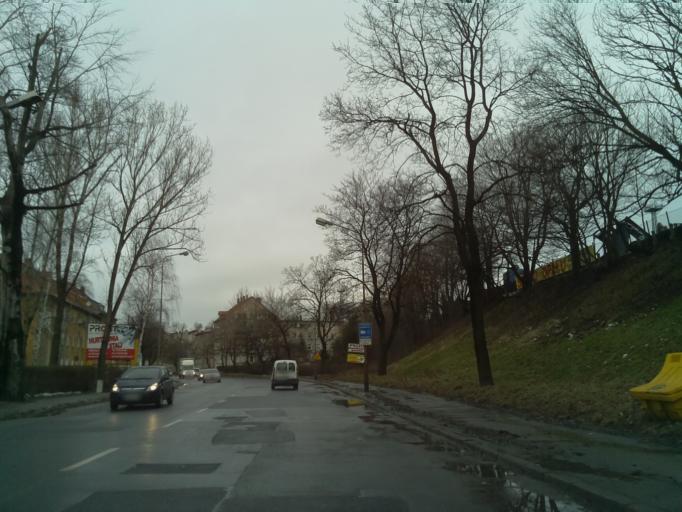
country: PL
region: Lower Silesian Voivodeship
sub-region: Powiat walbrzyski
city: Szczawno-Zdroj
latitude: 50.8154
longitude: 16.3010
